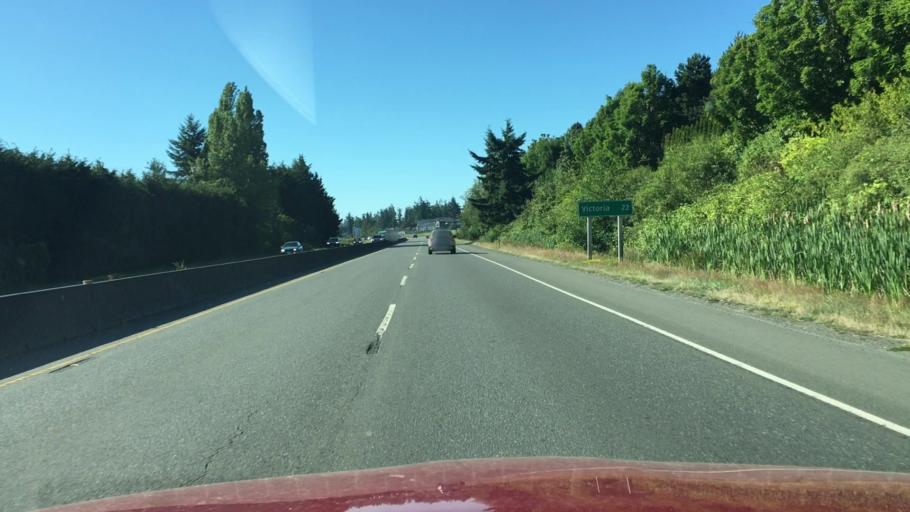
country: CA
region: British Columbia
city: North Saanich
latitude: 48.6243
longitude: -123.4099
